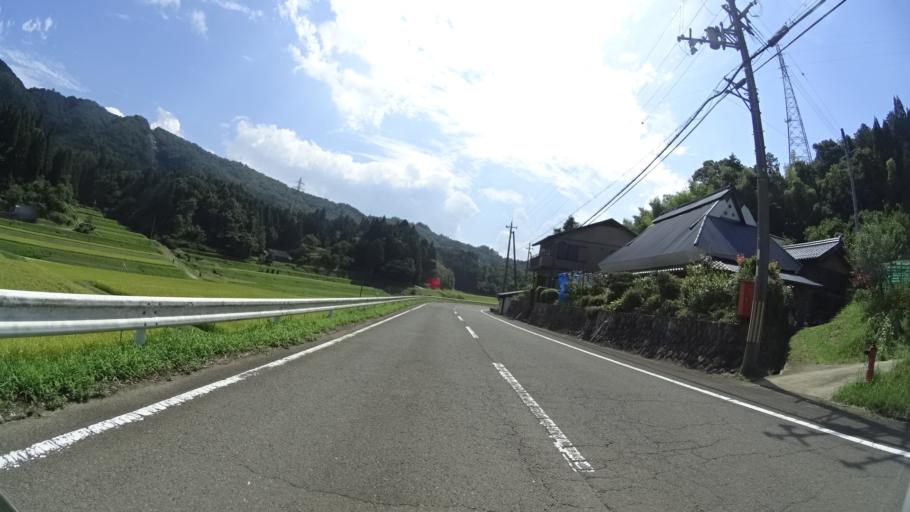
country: JP
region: Kyoto
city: Maizuru
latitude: 35.3702
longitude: 135.3378
